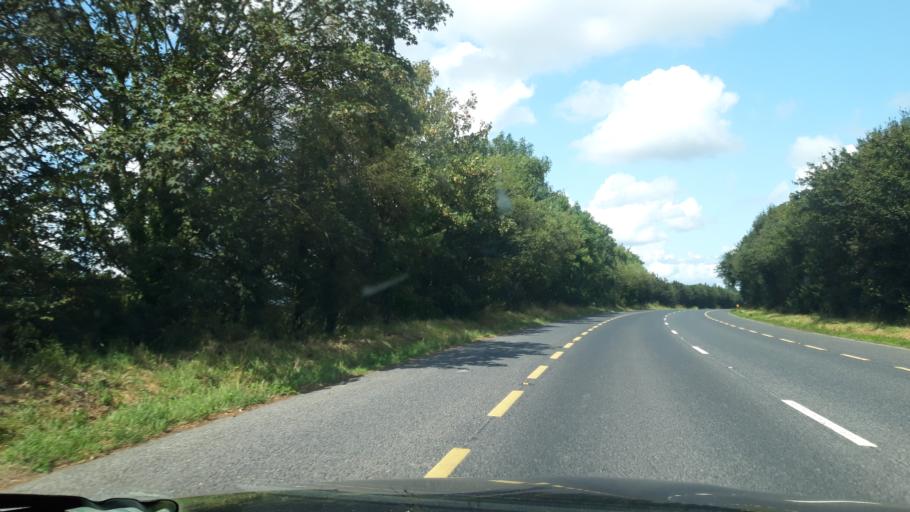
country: IE
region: Munster
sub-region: Waterford
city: Waterford
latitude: 52.2754
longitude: -7.0539
